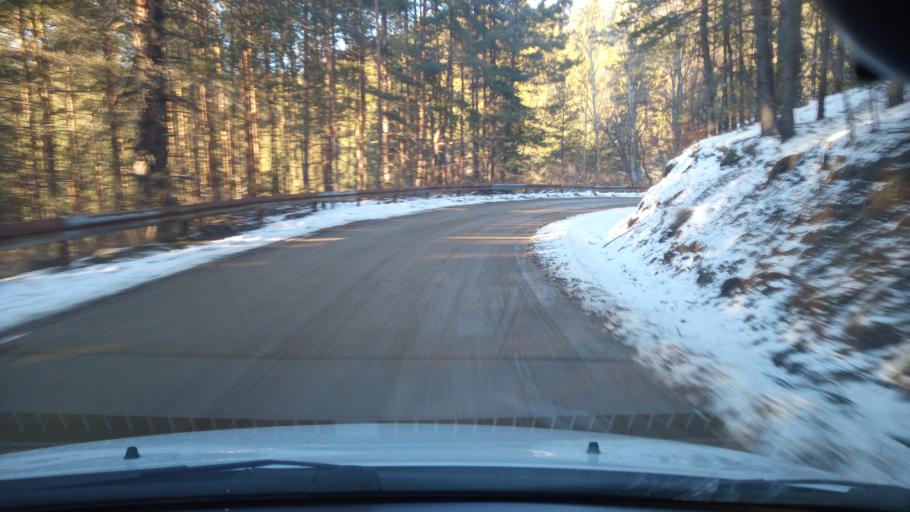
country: BG
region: Sofiya
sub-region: Obshtina Samokov
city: Samokov
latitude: 42.4821
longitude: 23.4100
